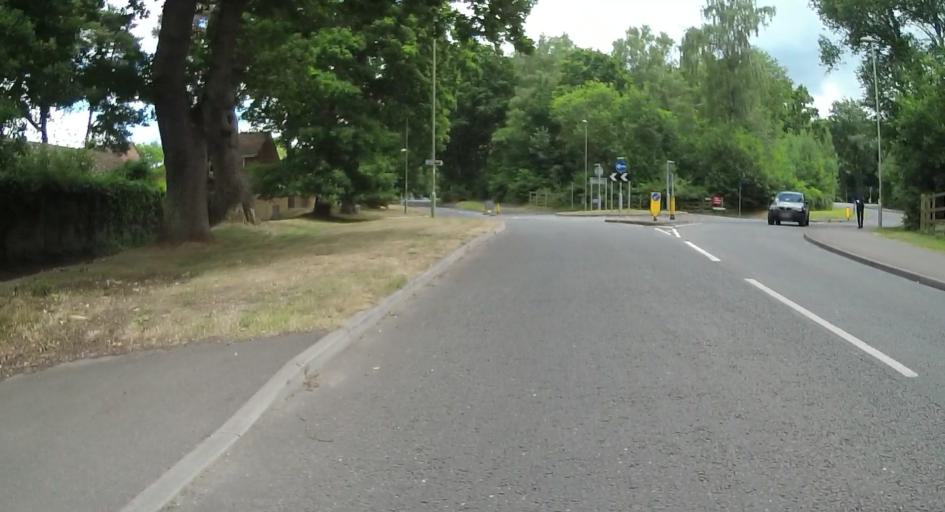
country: GB
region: England
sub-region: Hampshire
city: Fleet
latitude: 51.2581
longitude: -0.8303
